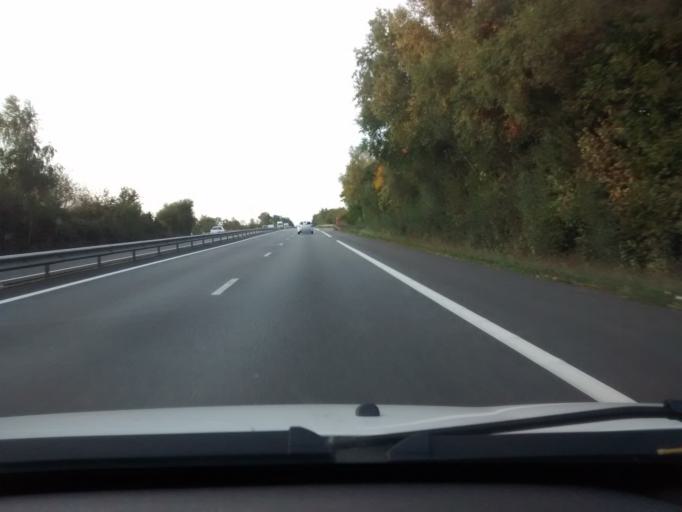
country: FR
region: Pays de la Loire
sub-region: Departement de la Loire-Atlantique
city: Derval
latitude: 47.6703
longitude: -1.6870
